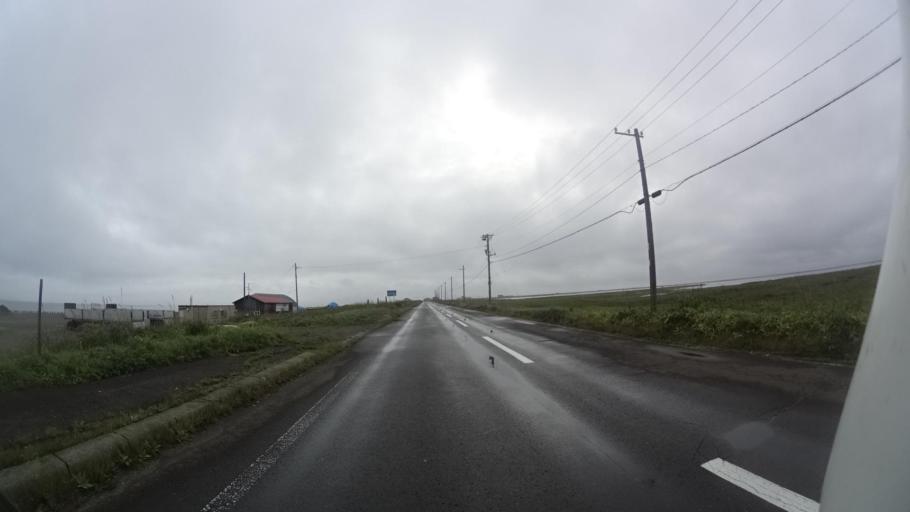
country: JP
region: Hokkaido
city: Shibetsu
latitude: 43.5985
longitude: 145.3168
